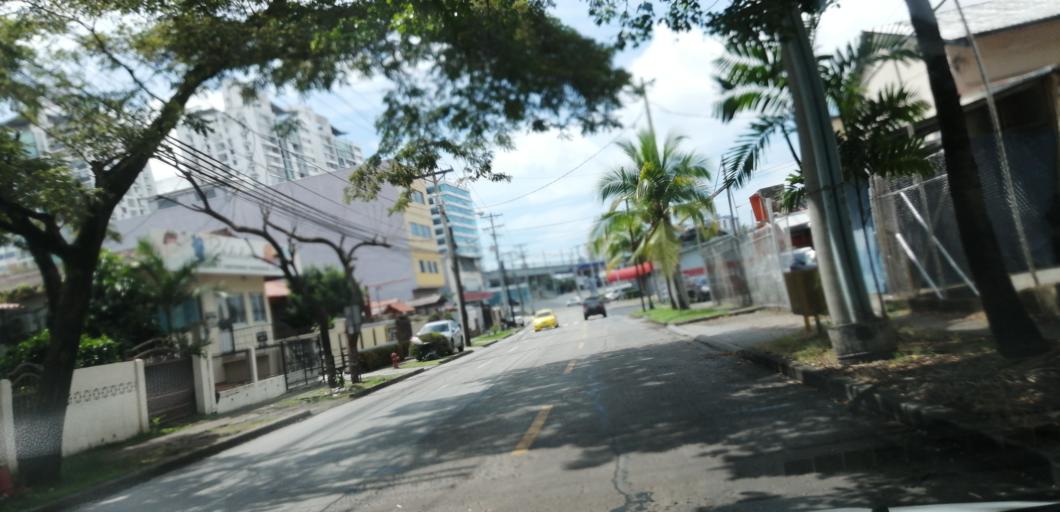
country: PA
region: Panama
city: Panama
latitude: 9.0208
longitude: -79.5177
